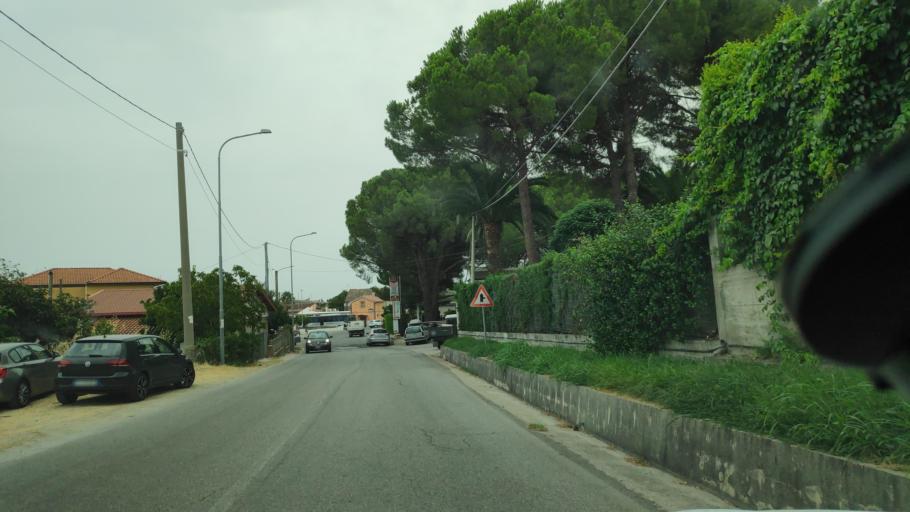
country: IT
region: Calabria
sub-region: Provincia di Catanzaro
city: Martelli-Laganosa
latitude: 38.6670
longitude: 16.5237
